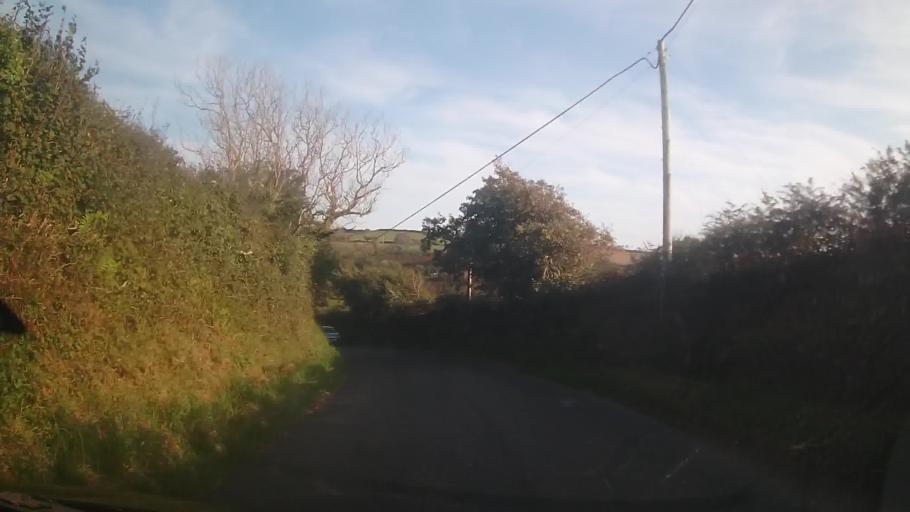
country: GB
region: Wales
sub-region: Pembrokeshire
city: Fishguard
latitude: 51.9849
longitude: -4.9553
